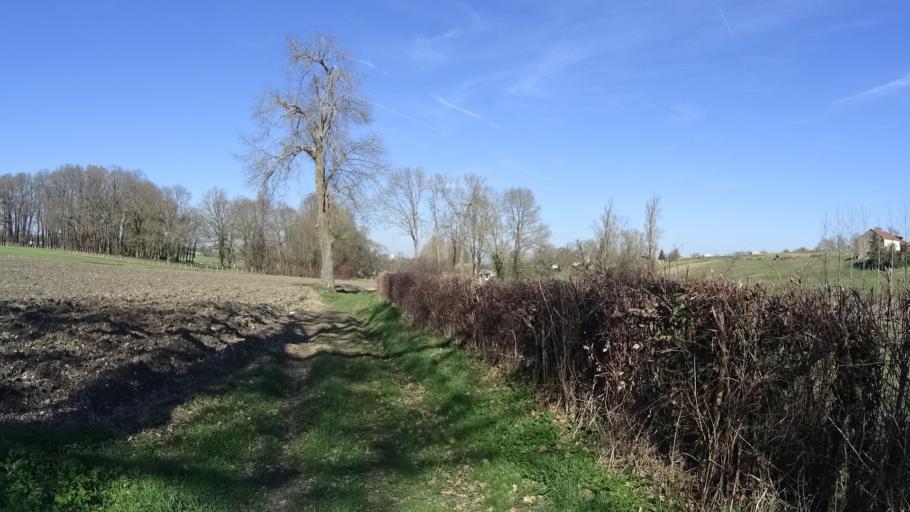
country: FR
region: Aquitaine
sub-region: Departement de la Dordogne
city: Riberac
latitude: 45.2263
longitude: 0.3335
